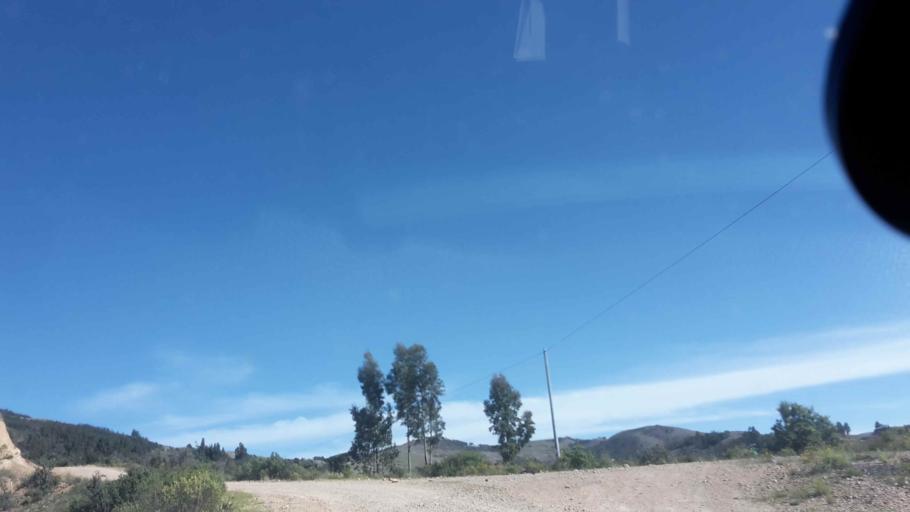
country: BO
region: Cochabamba
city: Arani
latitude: -17.6675
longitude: -65.7337
